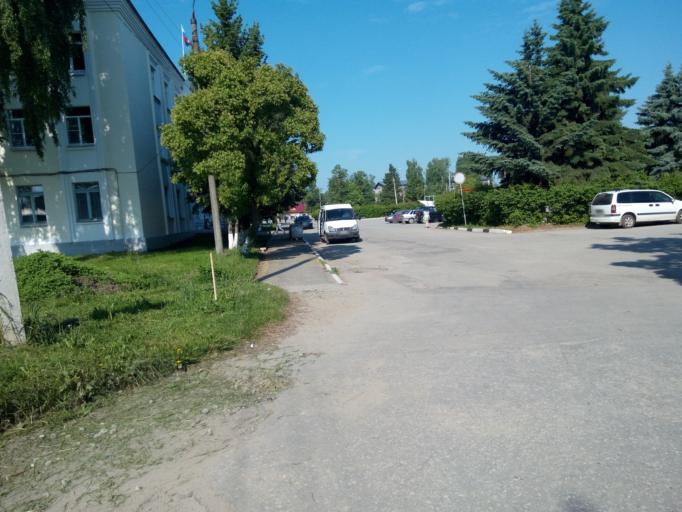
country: RU
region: Nizjnij Novgorod
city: Voskresenskoye
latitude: 56.8358
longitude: 45.4383
